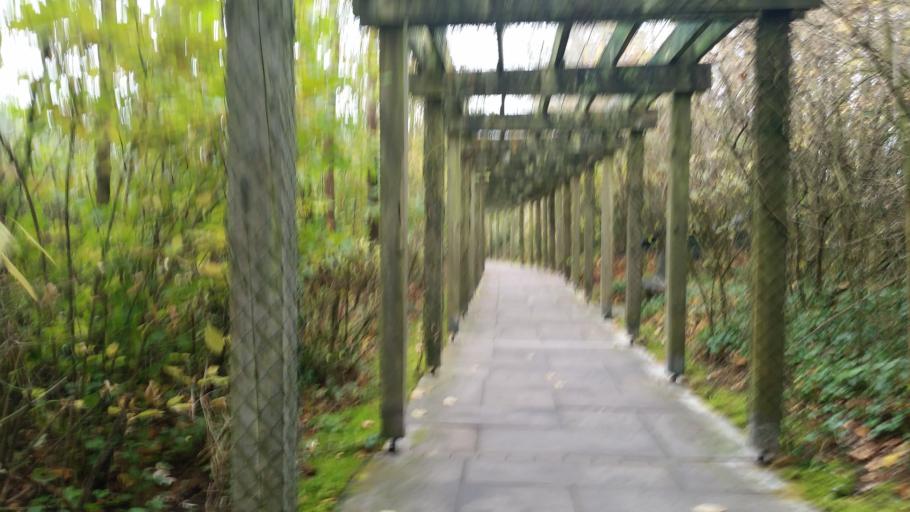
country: IE
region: Leinster
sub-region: An Mhi
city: Duleek
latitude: 53.6944
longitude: -6.4478
